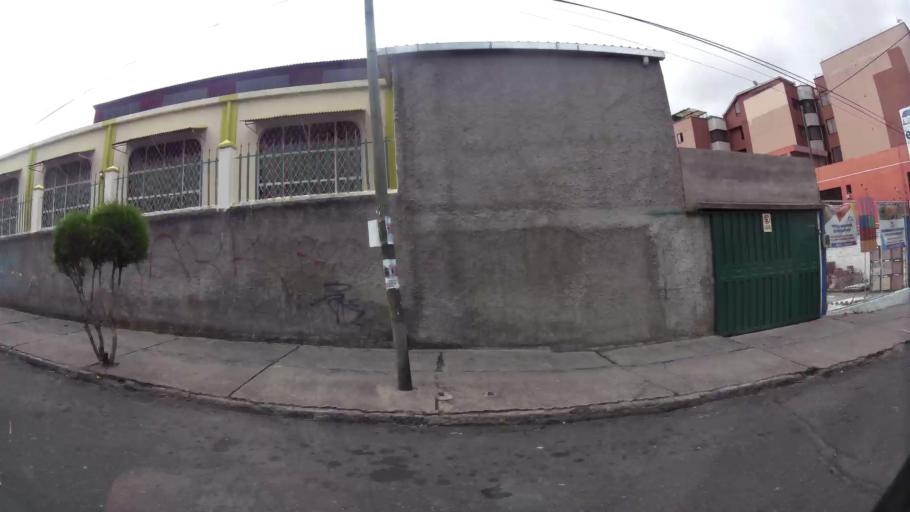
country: EC
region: Pichincha
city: Quito
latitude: -0.1293
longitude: -78.4951
